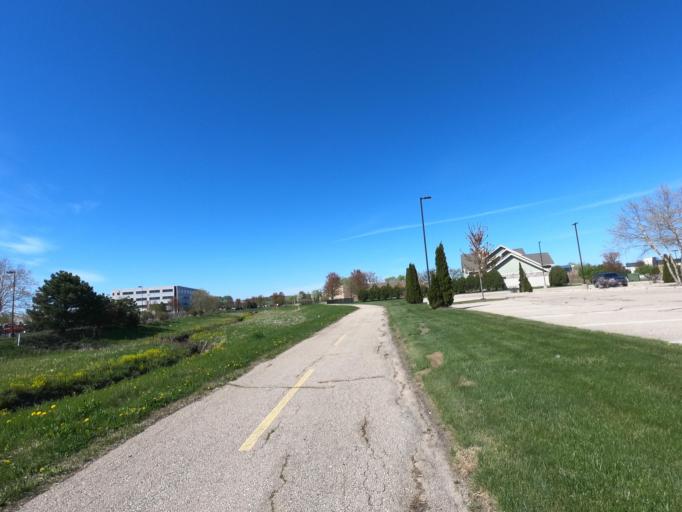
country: US
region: Wisconsin
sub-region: Dane County
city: Middleton
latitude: 43.1000
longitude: -89.5213
